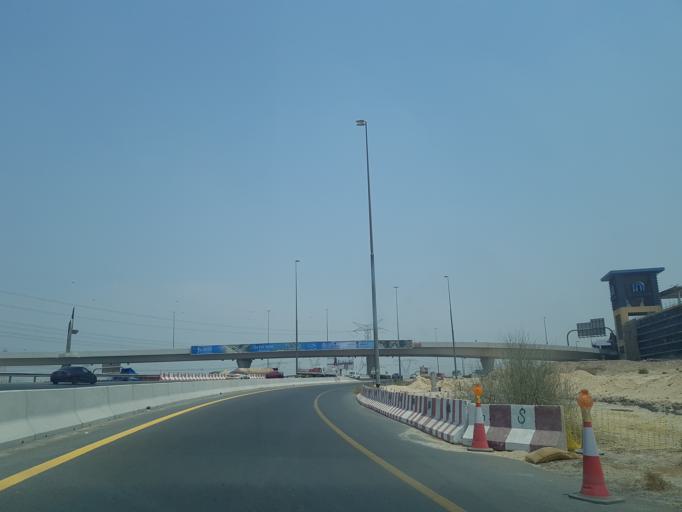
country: AE
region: Ash Shariqah
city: Sharjah
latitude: 25.2145
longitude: 55.4049
